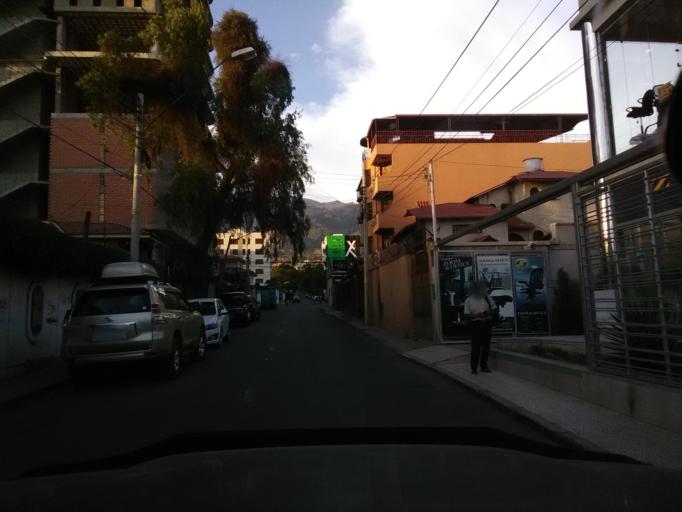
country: BO
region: Cochabamba
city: Cochabamba
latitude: -17.3737
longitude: -66.1548
